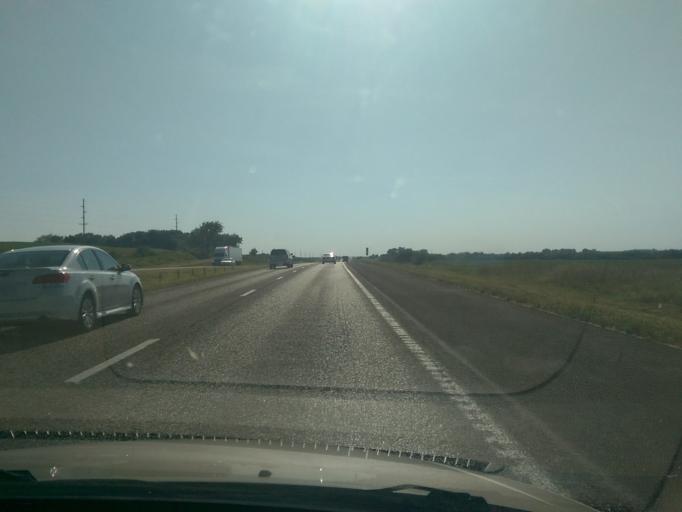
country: US
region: Missouri
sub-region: Lafayette County
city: Concordia
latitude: 38.9914
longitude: -93.6137
